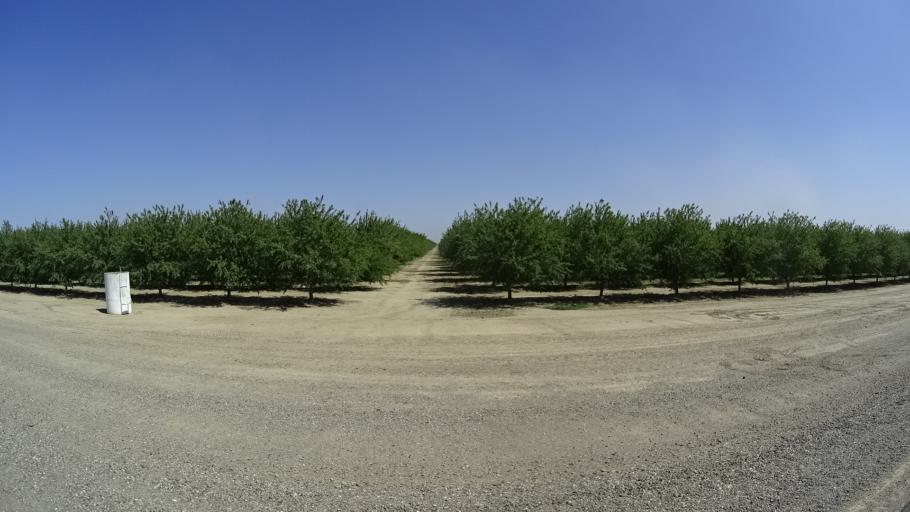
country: US
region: California
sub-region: Glenn County
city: Willows
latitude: 39.5857
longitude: -122.1371
